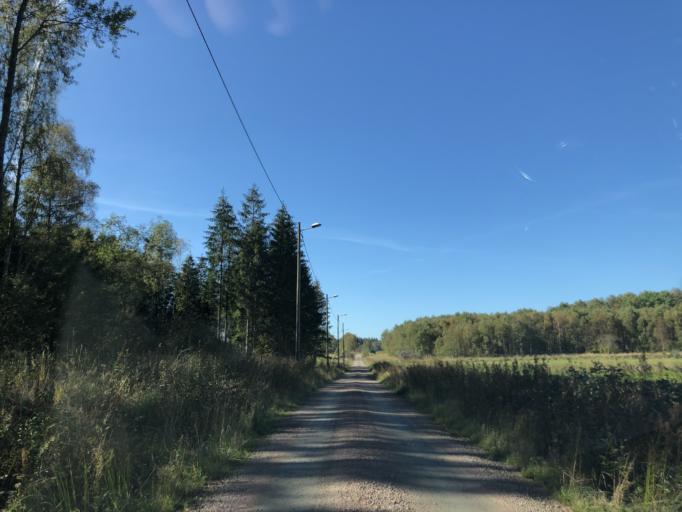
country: SE
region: Vaestra Goetaland
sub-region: Goteborg
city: Majorna
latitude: 57.7647
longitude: 11.9143
